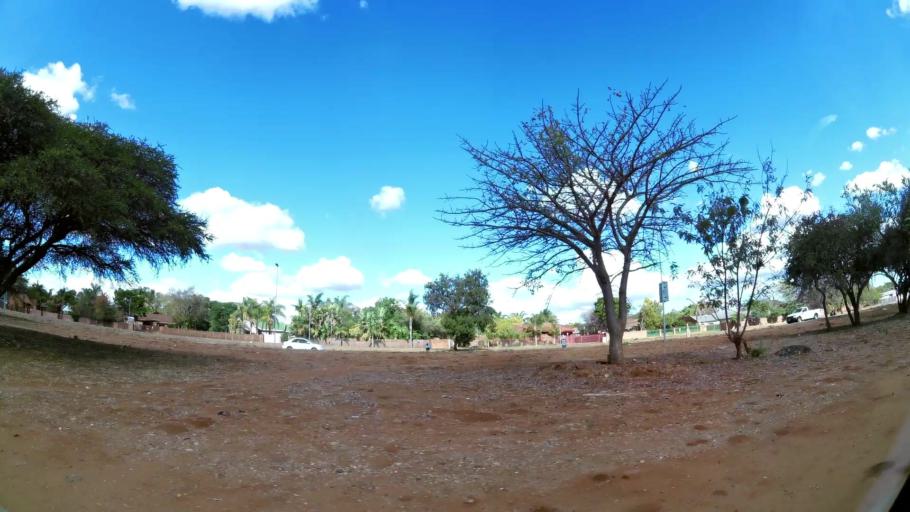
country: ZA
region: Limpopo
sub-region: Capricorn District Municipality
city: Polokwane
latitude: -23.8966
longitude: 29.4826
